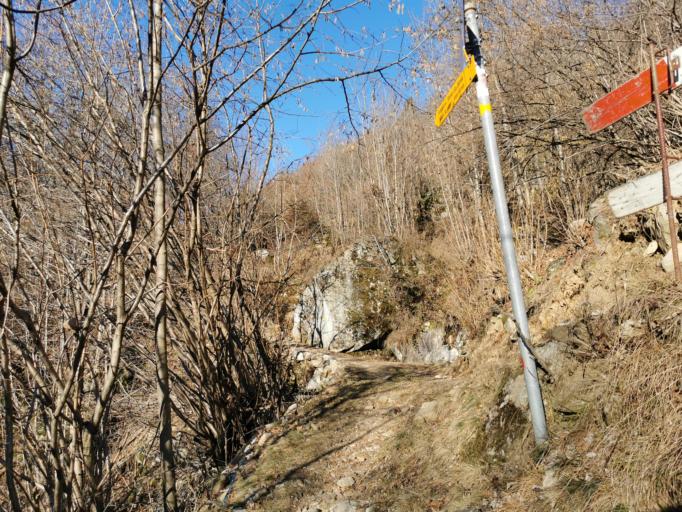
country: CH
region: Ticino
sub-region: Leventina District
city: Faido
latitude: 46.4922
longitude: 8.7729
